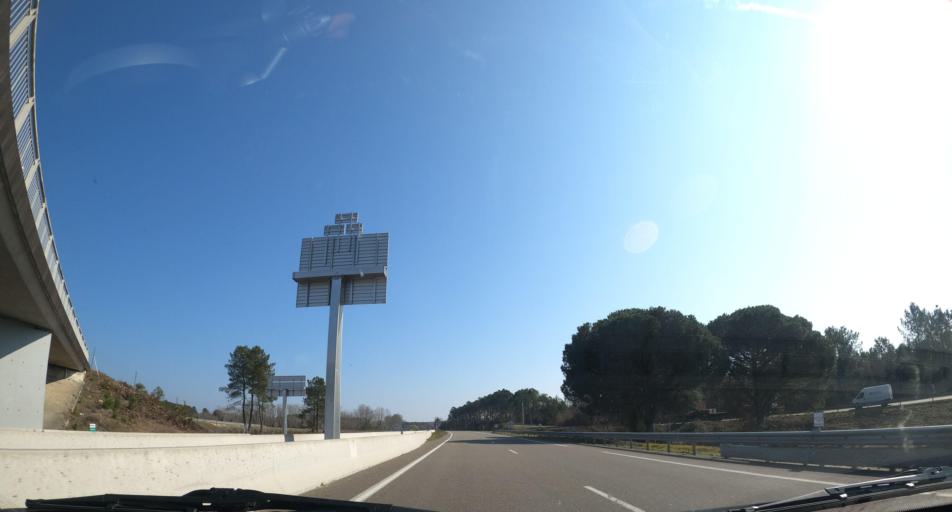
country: FR
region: Aquitaine
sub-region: Departement des Landes
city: Saint-Geours-de-Maremne
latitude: 43.6949
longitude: -1.2065
